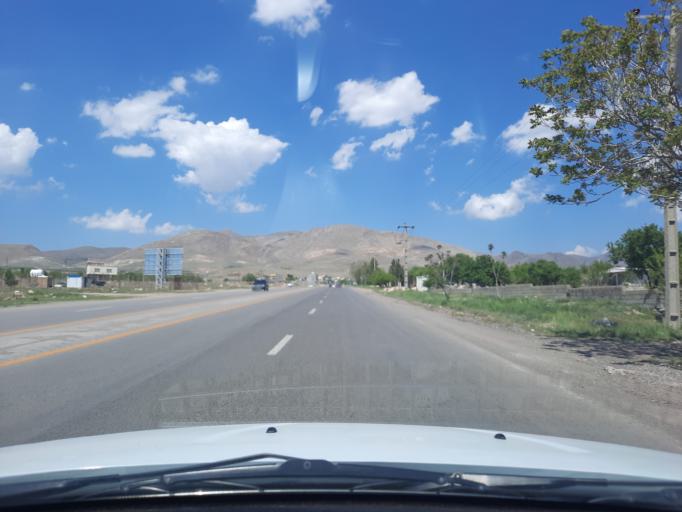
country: IR
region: Qazvin
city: Qazvin
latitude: 36.3237
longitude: 50.1477
